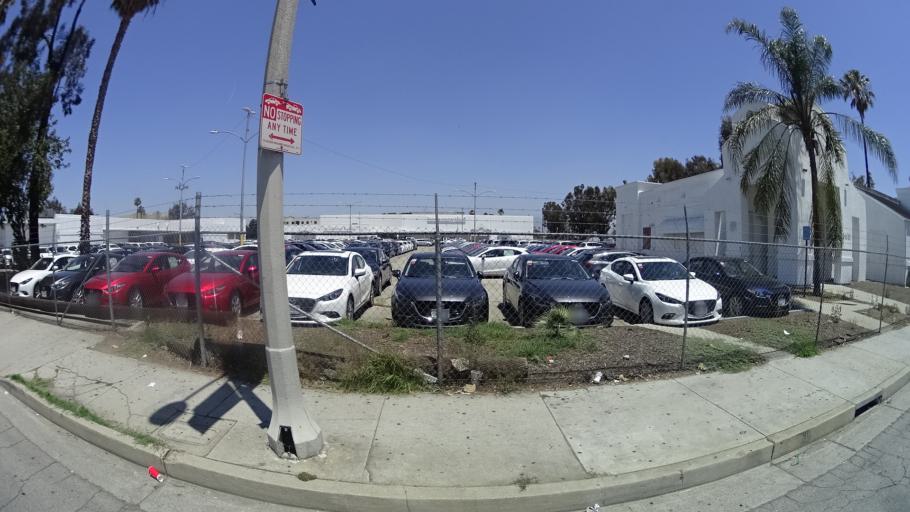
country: US
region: California
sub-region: Los Angeles County
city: Van Nuys
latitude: 34.2216
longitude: -118.4522
